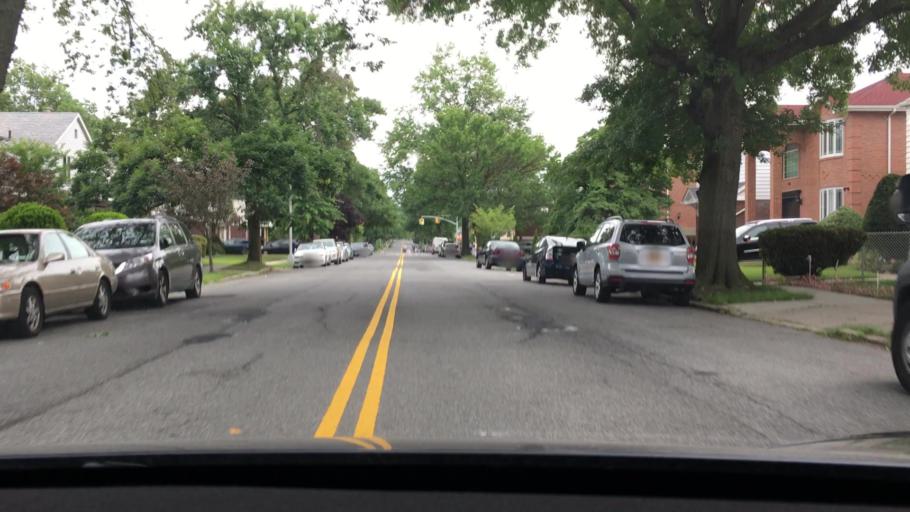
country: US
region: New York
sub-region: Queens County
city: Jamaica
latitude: 40.7315
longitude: -73.7782
